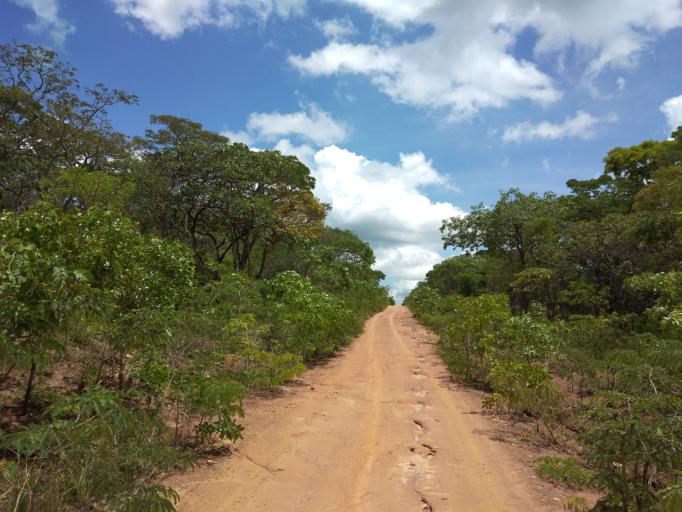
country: ZM
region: Central
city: Mkushi
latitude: -13.9824
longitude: 29.9426
